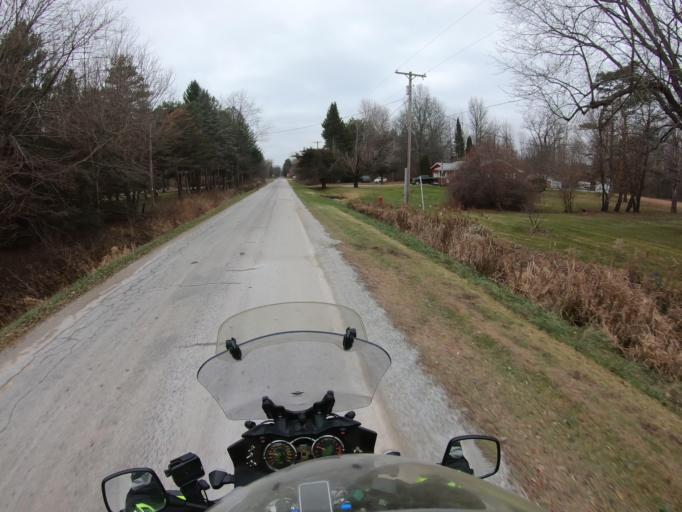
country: US
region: Michigan
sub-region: Saginaw County
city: Saint Charles
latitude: 43.3441
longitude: -84.1329
